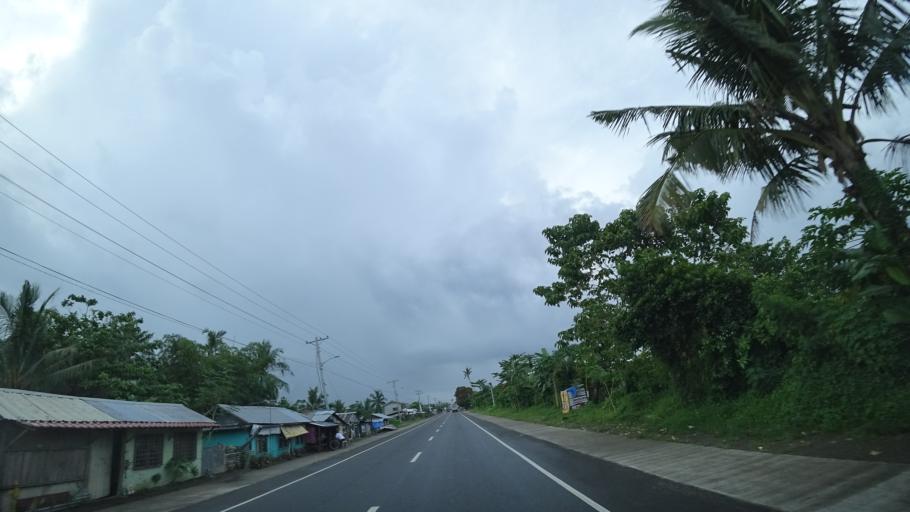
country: PH
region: Eastern Visayas
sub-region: Province of Leyte
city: Bislig
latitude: 11.0702
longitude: 125.0341
